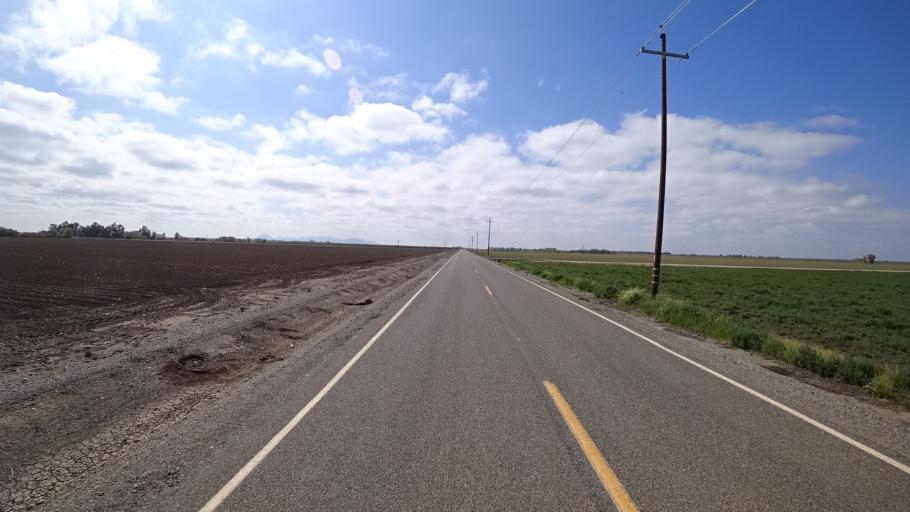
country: US
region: California
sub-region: Butte County
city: Biggs
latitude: 39.4248
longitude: -121.9295
